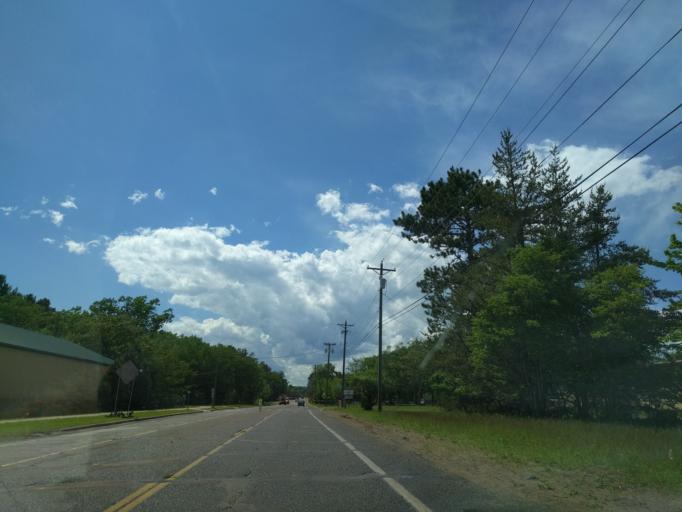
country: US
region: Michigan
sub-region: Marquette County
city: Trowbridge Park
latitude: 46.5640
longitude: -87.4152
